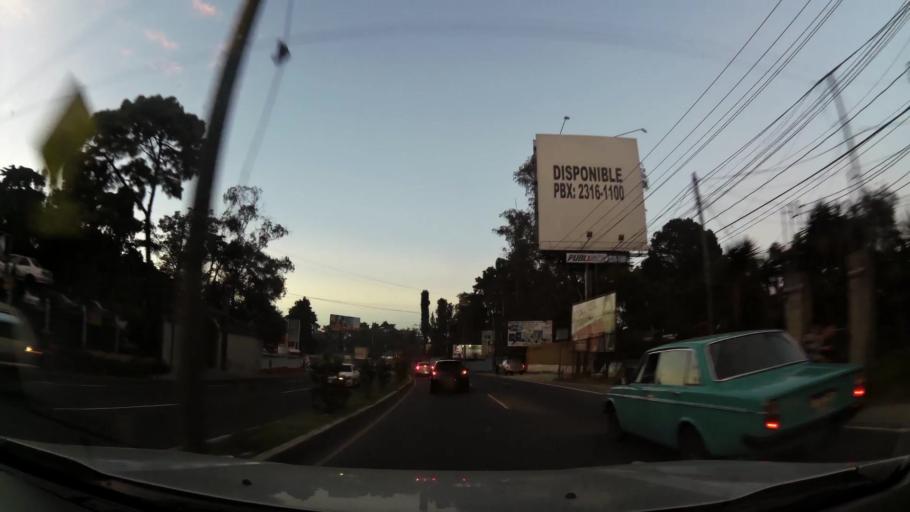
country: GT
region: Guatemala
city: Mixco
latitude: 14.6223
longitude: -90.6046
